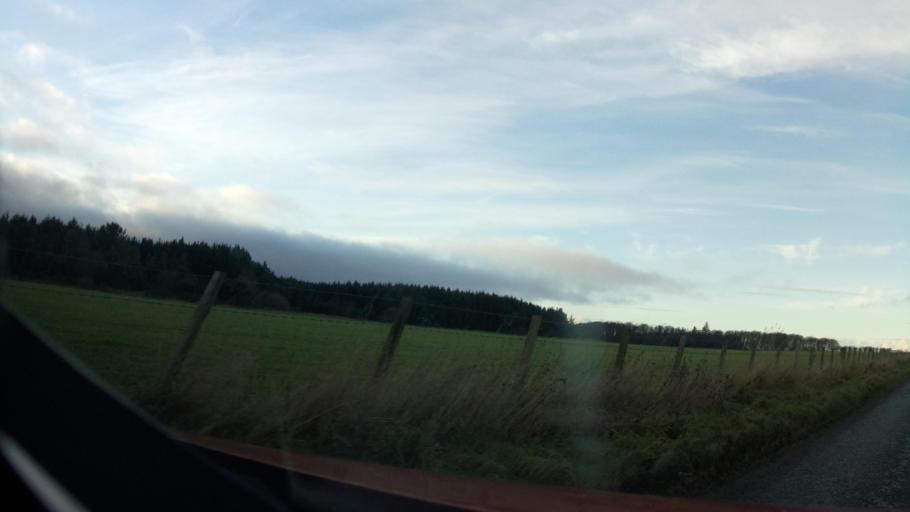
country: GB
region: Scotland
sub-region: Angus
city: Letham
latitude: 56.5569
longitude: -2.7655
